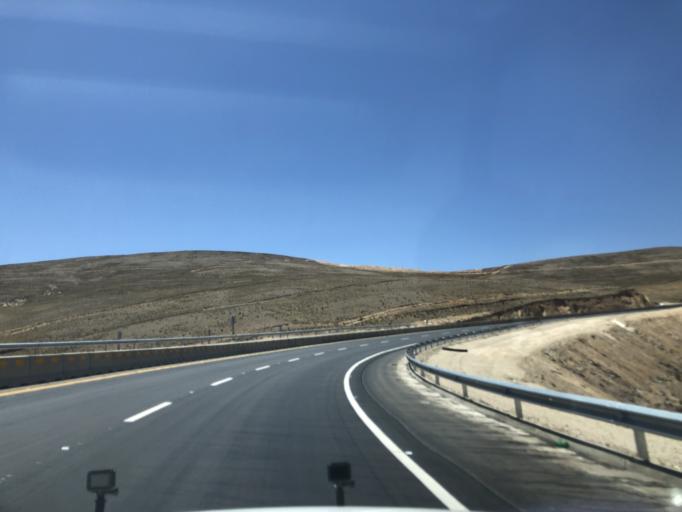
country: BO
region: Cochabamba
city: Colchani
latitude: -17.6658
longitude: -66.7589
